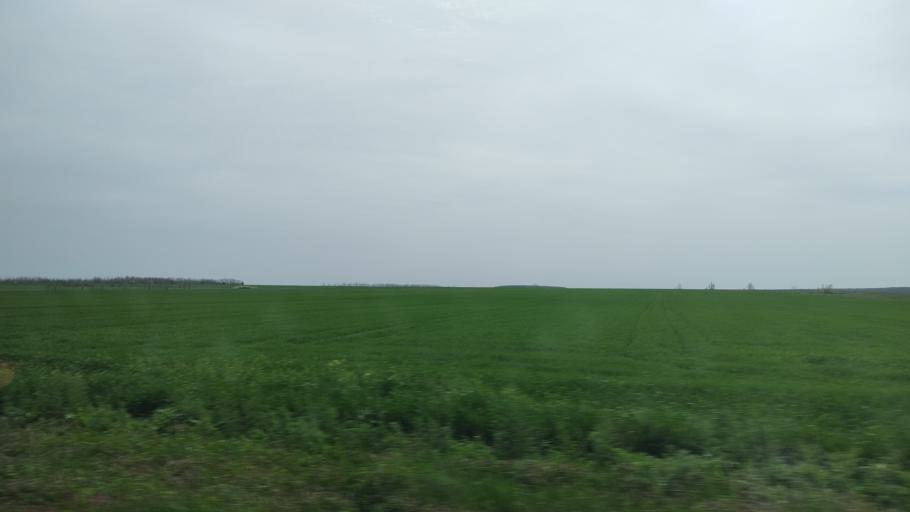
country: RO
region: Constanta
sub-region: Comuna Ciocarlia
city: Ciocarlia
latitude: 44.0851
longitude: 28.2531
